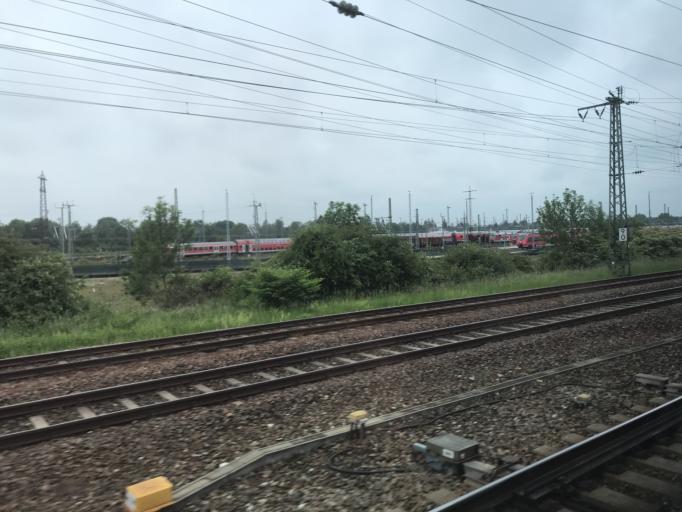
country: DE
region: Bavaria
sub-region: Upper Bavaria
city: Pasing
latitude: 48.1566
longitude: 11.4434
